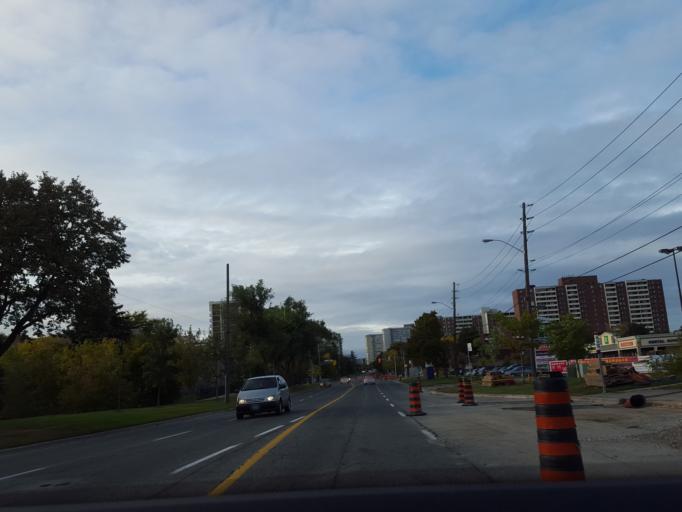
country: CA
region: Ontario
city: Scarborough
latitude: 43.7906
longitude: -79.3131
